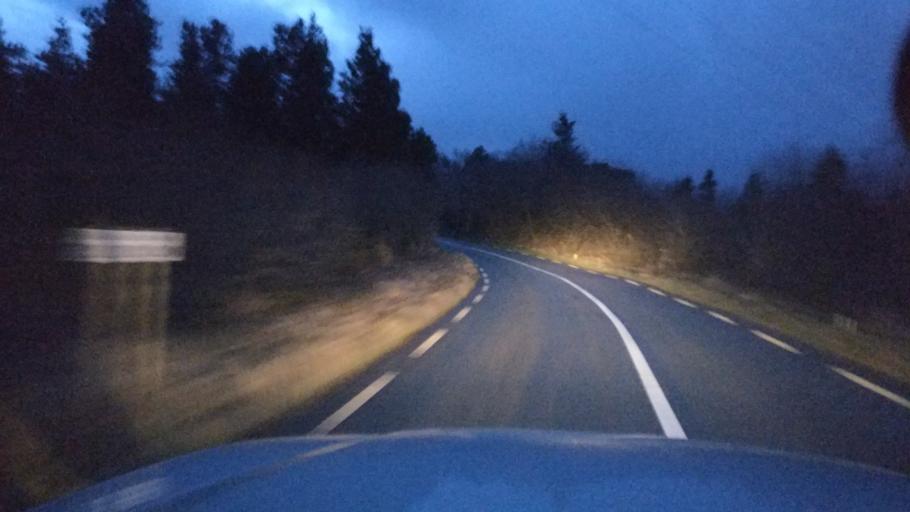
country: IE
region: Connaught
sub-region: County Galway
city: Oughterard
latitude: 53.3883
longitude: -9.5496
